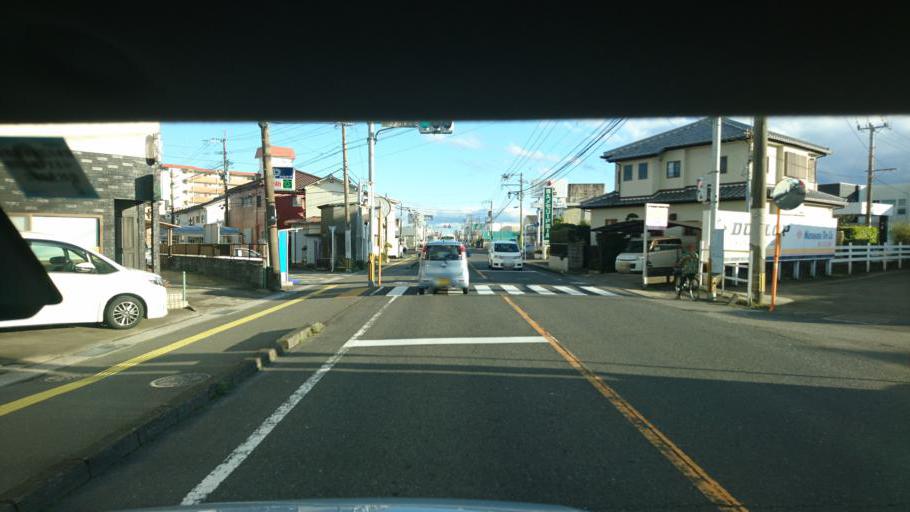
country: JP
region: Miyazaki
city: Miyazaki-shi
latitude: 31.8906
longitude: 131.4214
